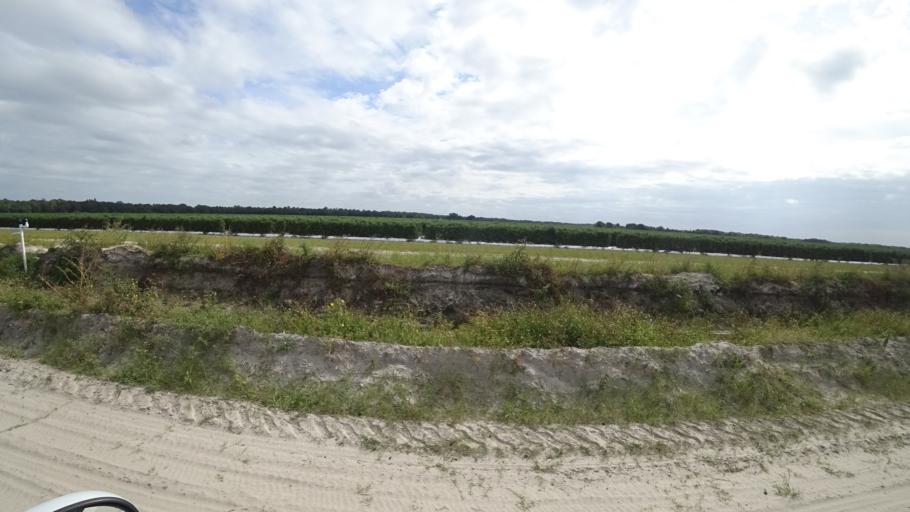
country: US
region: Florida
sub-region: Hillsborough County
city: Wimauma
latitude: 27.5892
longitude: -82.3121
